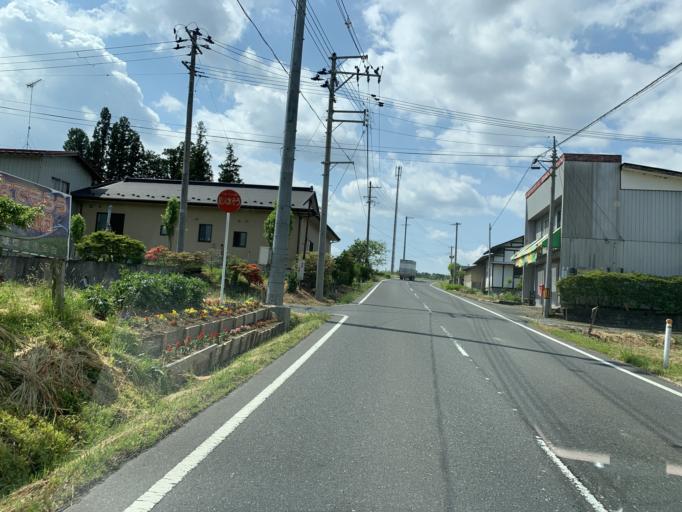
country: JP
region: Miyagi
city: Furukawa
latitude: 38.7852
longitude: 140.9580
